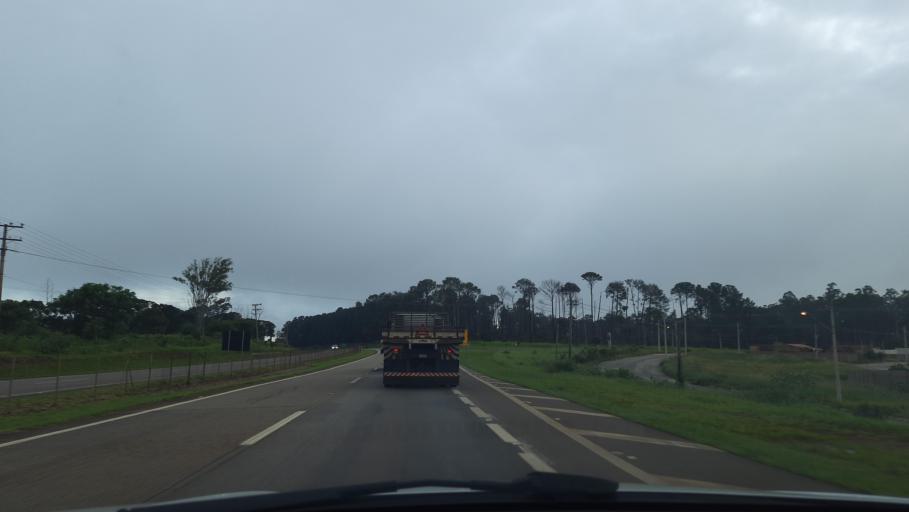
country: BR
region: Sao Paulo
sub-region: Casa Branca
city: Casa Branca
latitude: -21.7631
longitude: -47.0700
